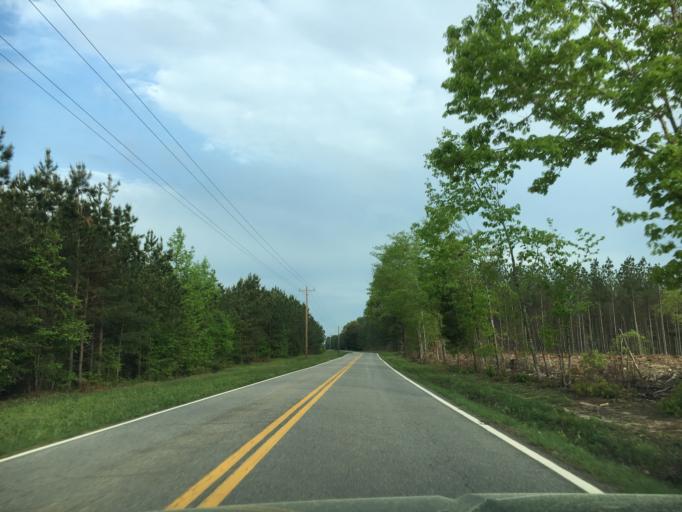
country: US
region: Virginia
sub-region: Halifax County
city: Halifax
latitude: 36.8922
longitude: -78.8125
